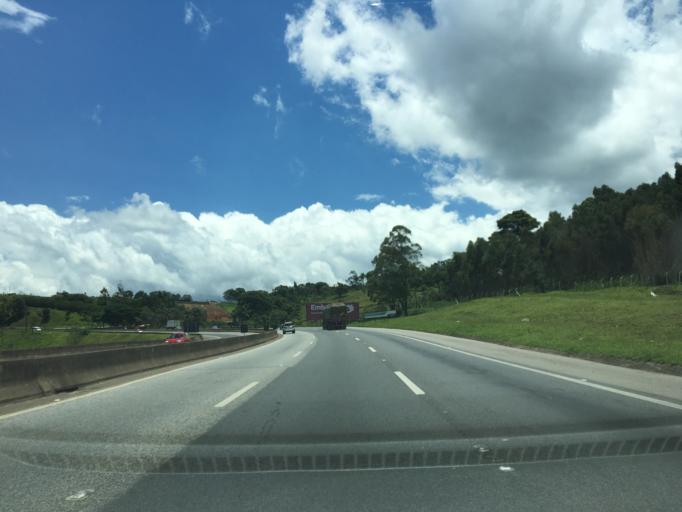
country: BR
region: Sao Paulo
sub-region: Mairipora
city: Mairipora
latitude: -23.2507
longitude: -46.5938
